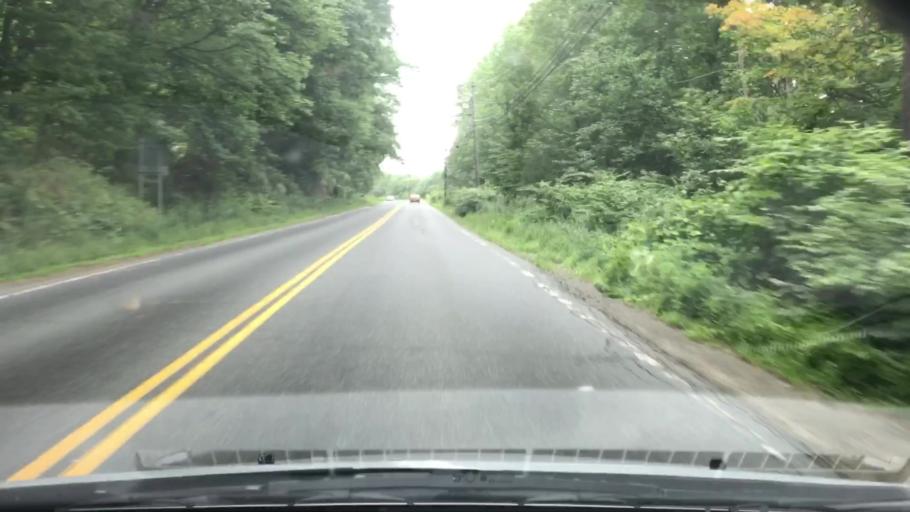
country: US
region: New Hampshire
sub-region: Grafton County
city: Woodsville
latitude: 44.1296
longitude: -72.0314
